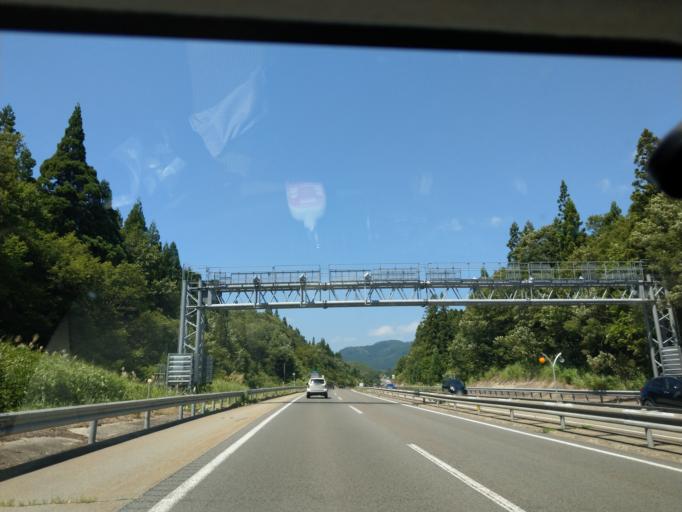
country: JP
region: Akita
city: Omagari
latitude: 39.4130
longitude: 140.4391
